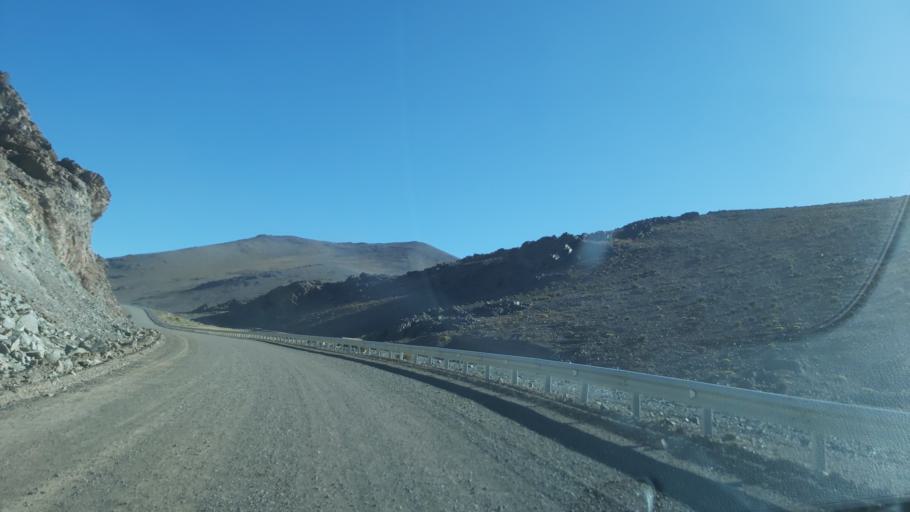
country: CL
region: Atacama
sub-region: Provincia de Chanaral
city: Diego de Almagro
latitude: -26.4039
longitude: -69.2831
